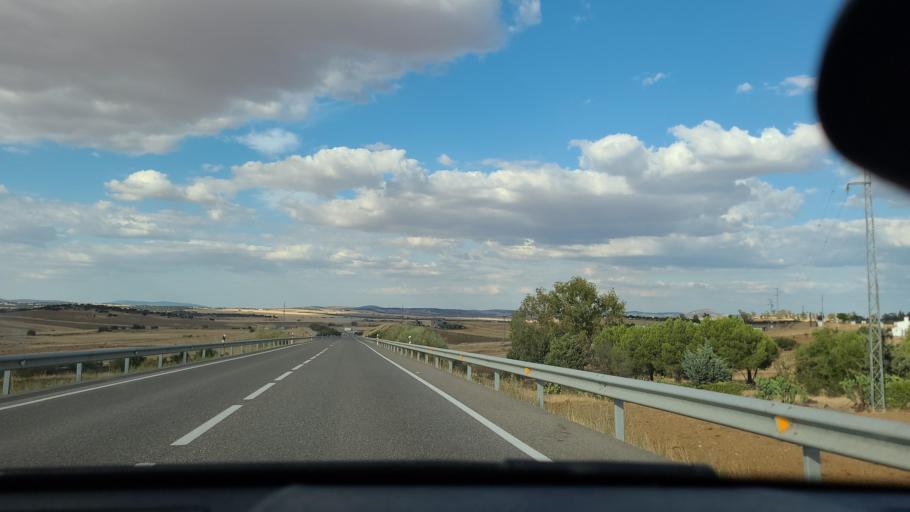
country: ES
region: Andalusia
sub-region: Province of Cordoba
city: Fuente Obejuna
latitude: 38.2689
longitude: -5.4329
